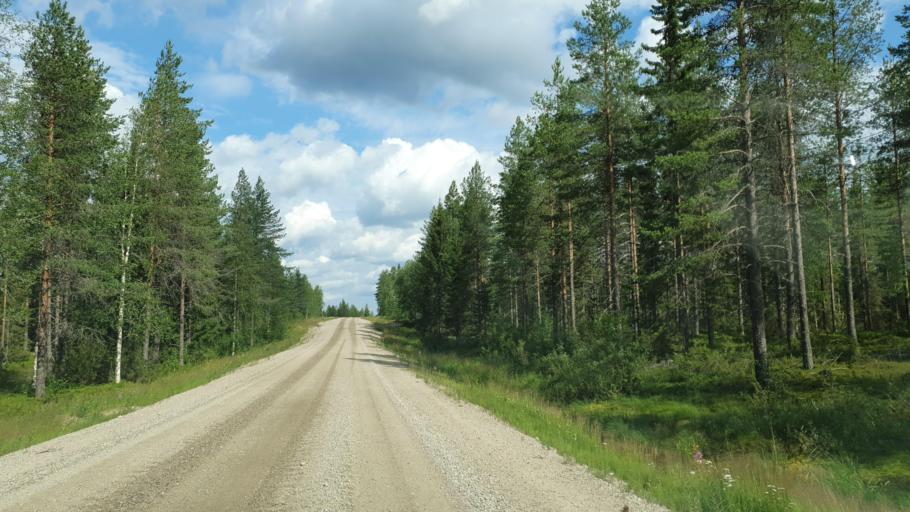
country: FI
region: Kainuu
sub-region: Kehys-Kainuu
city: Kuhmo
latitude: 64.4776
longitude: 29.5927
